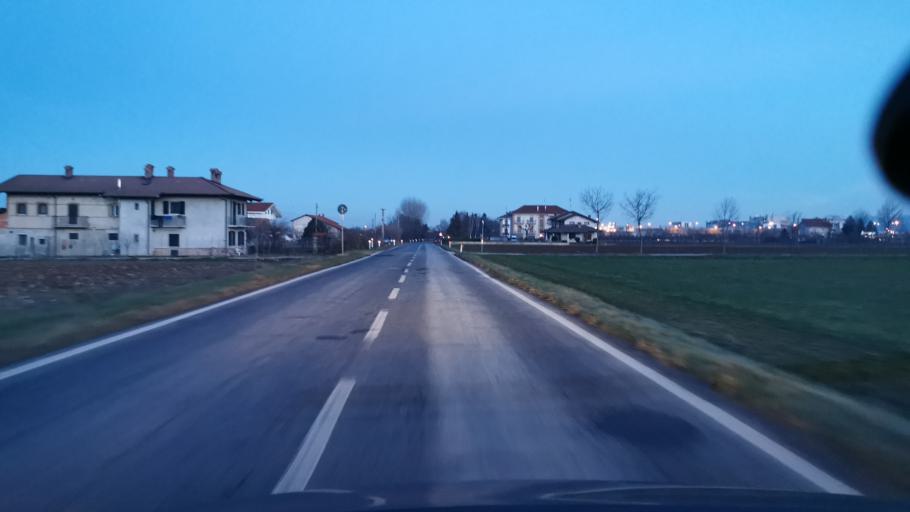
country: IT
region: Piedmont
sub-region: Provincia di Cuneo
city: Roata Rossi
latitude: 44.4423
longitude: 7.5581
